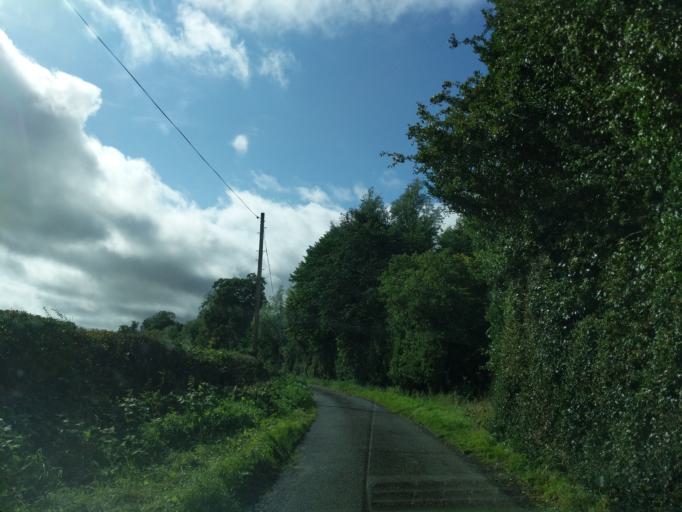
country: GB
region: Scotland
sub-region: The Scottish Borders
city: Kelso
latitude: 55.5707
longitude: -2.4704
